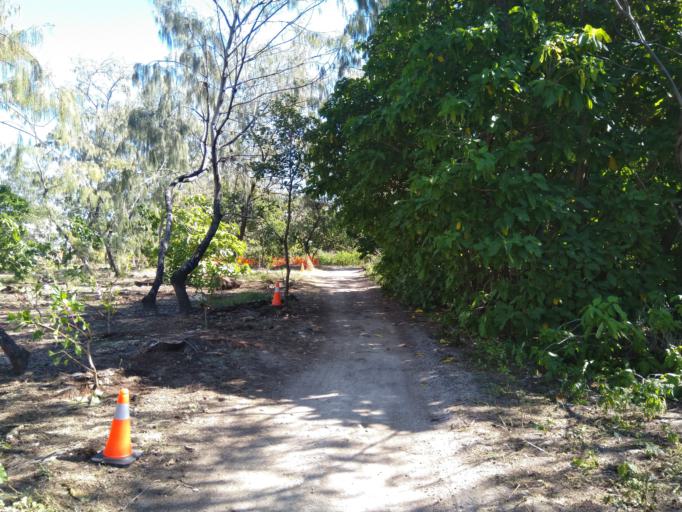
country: AU
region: Queensland
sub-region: Bundaberg
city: Bundaberg
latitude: -24.1135
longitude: 152.7132
